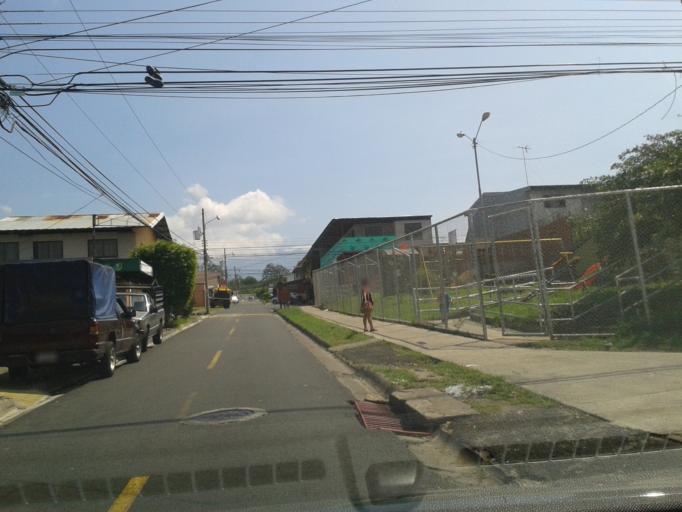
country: CR
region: Heredia
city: San Francisco
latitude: 9.9864
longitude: -84.1361
